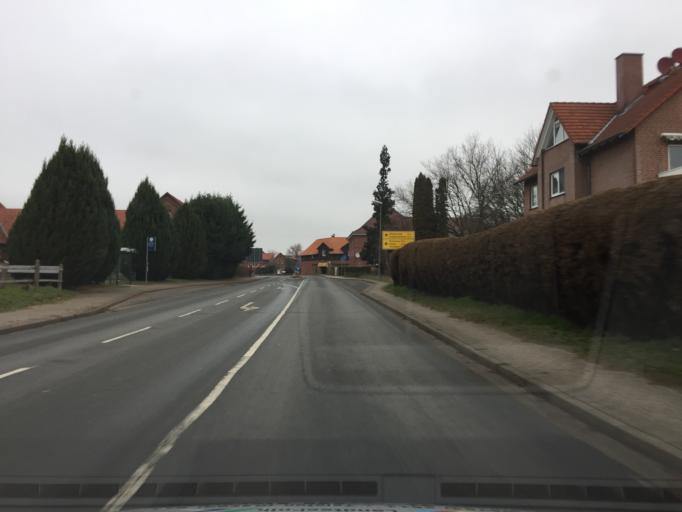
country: DE
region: Lower Saxony
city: Meerbeck
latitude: 52.3414
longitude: 9.1455
